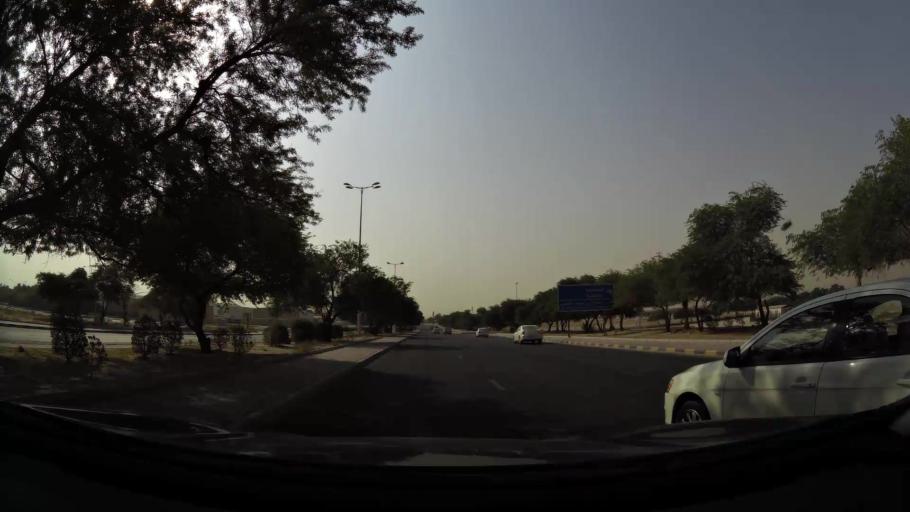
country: KW
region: Al Asimah
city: Ar Rabiyah
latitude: 29.2912
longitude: 47.8319
